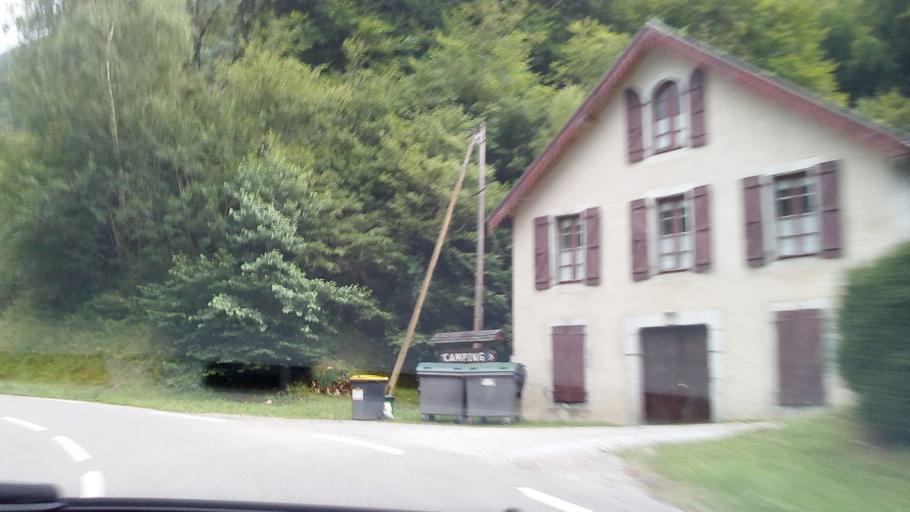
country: FR
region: Aquitaine
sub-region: Departement des Pyrenees-Atlantiques
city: Laruns
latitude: 42.9696
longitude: -0.3816
